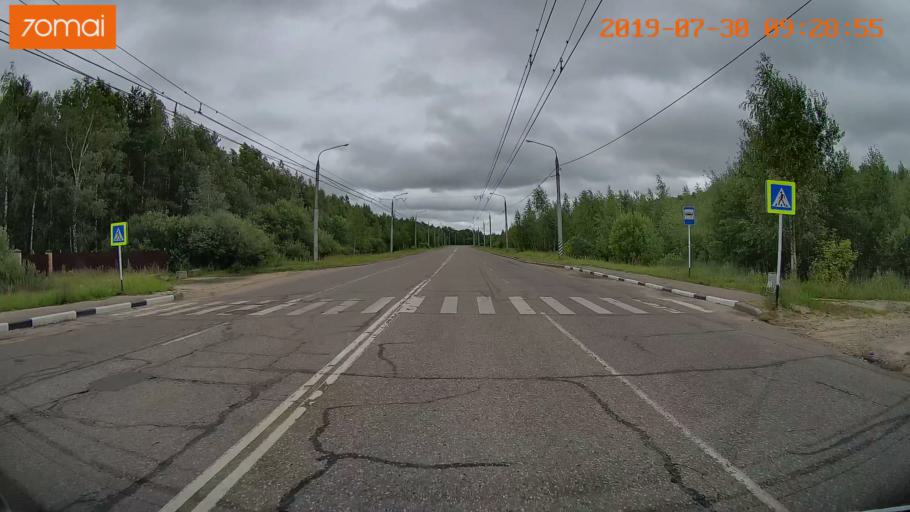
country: RU
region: Ivanovo
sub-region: Gorod Ivanovo
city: Ivanovo
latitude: 56.9492
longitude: 40.9472
